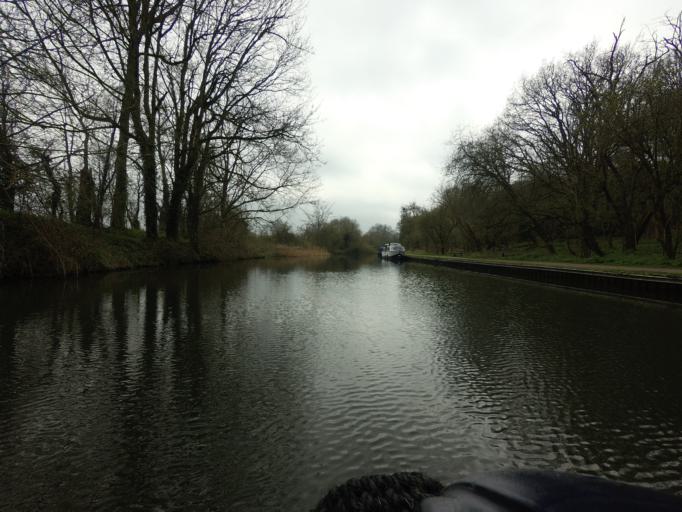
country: GB
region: England
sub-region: Hertfordshire
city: Watford
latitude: 51.6677
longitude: -0.4277
